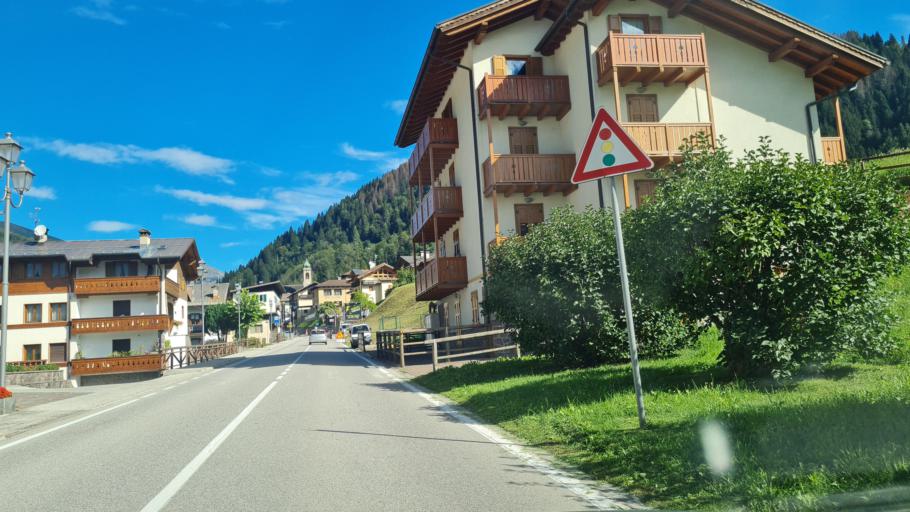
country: IT
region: Trentino-Alto Adige
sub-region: Provincia di Trento
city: Siror
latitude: 46.1860
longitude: 11.8308
